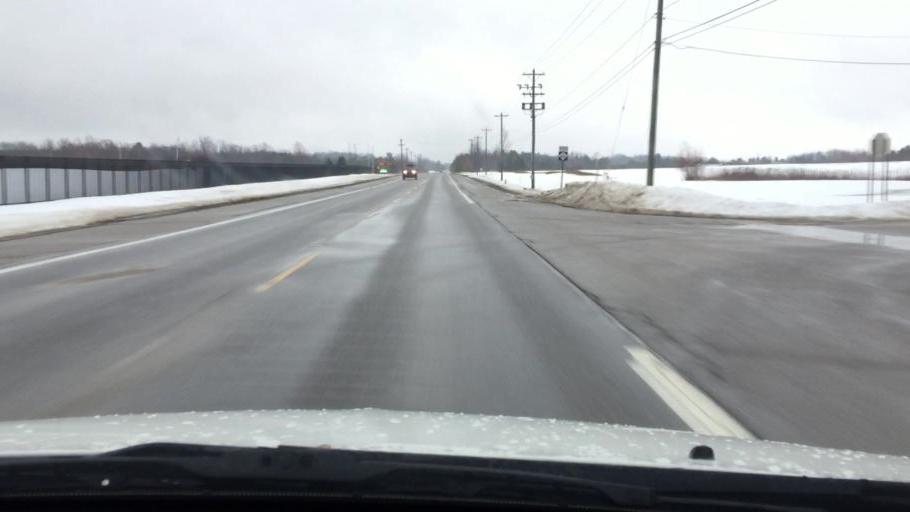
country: US
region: Michigan
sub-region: Charlevoix County
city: Charlevoix
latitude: 45.2795
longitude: -85.2313
